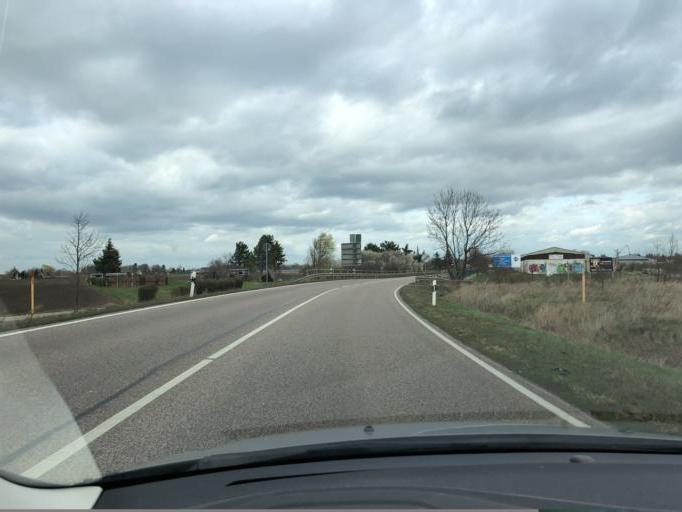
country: DE
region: Saxony-Anhalt
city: Lutzen
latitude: 51.2470
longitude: 12.1293
